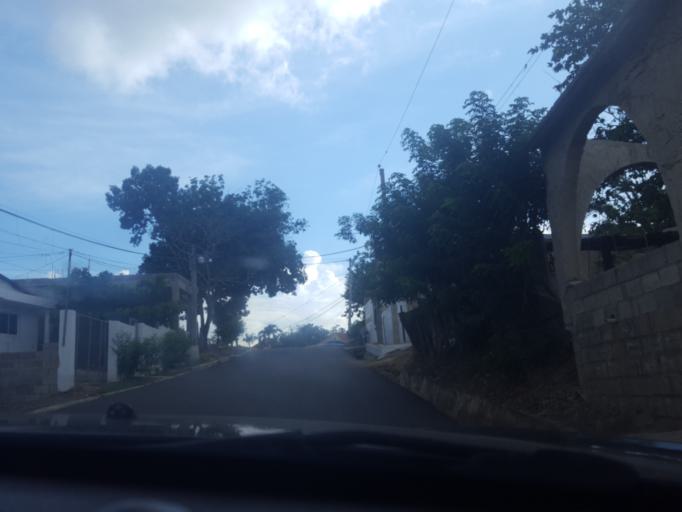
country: DO
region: Santiago
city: Licey al Medio
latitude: 19.3645
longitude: -70.6320
